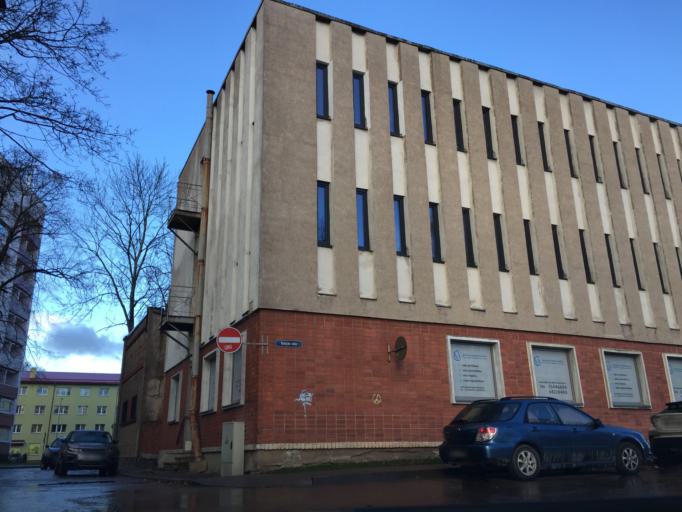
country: LV
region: Valmieras Rajons
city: Valmiera
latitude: 57.5358
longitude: 25.4204
